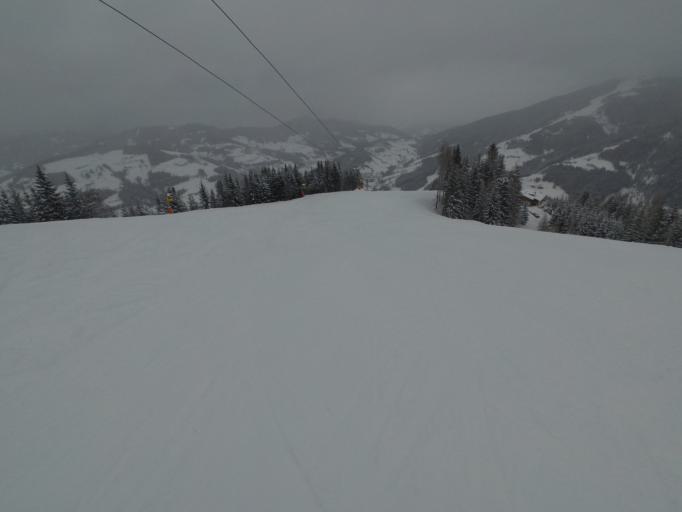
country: AT
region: Salzburg
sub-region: Politischer Bezirk Sankt Johann im Pongau
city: Wagrain
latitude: 47.3185
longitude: 13.2871
